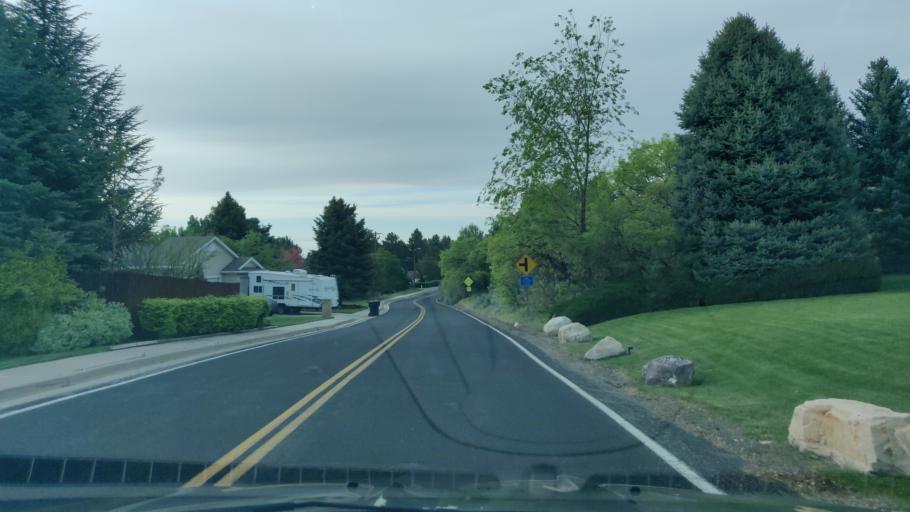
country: US
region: Utah
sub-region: Salt Lake County
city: Granite
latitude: 40.5931
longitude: -111.8002
